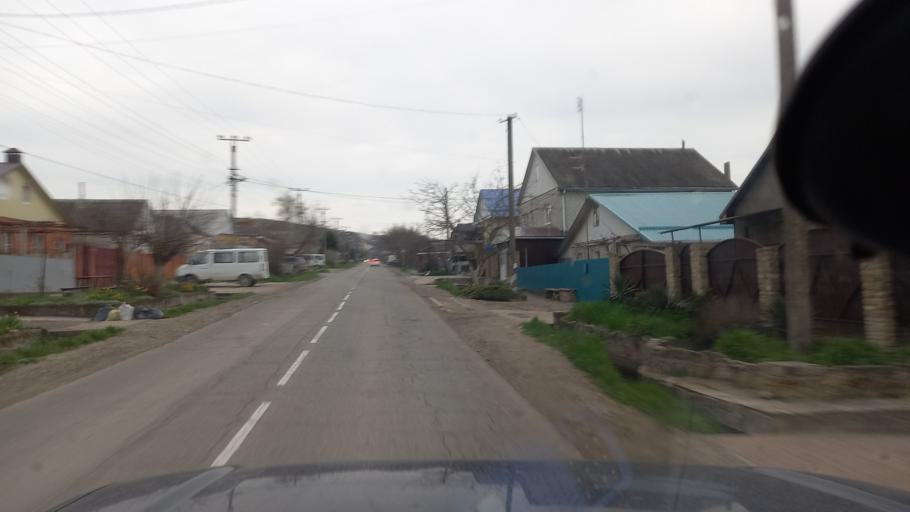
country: RU
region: Krasnodarskiy
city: Sukko
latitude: 44.8519
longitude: 37.4365
